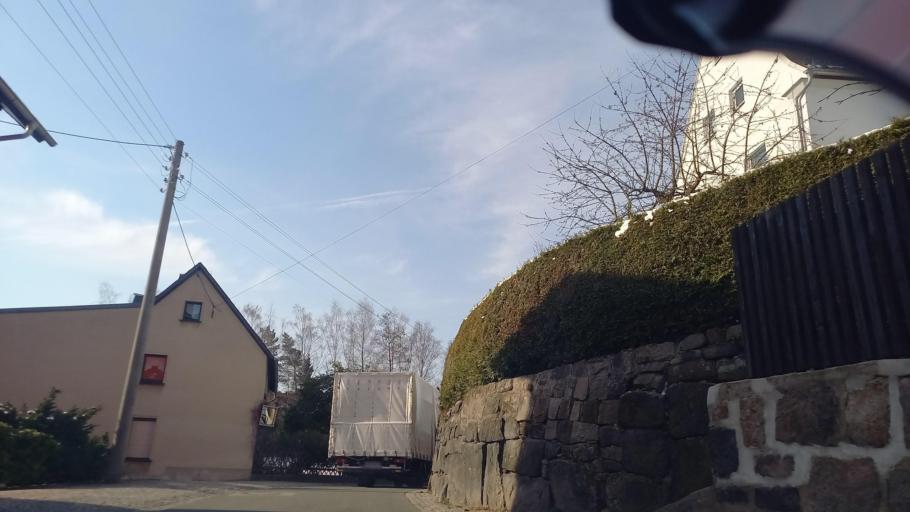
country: DE
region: Saxony
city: Stutzengrun
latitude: 50.5677
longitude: 12.4821
